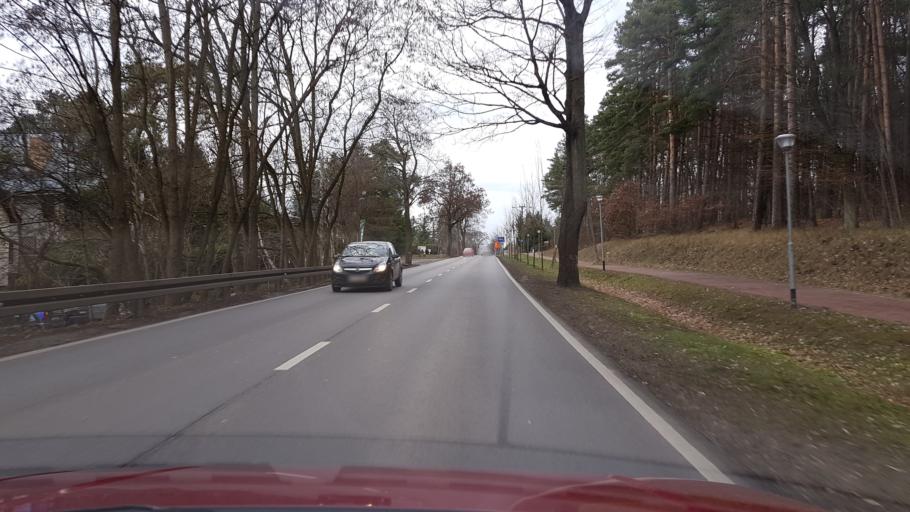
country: PL
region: West Pomeranian Voivodeship
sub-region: Szczecin
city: Szczecin
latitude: 53.4901
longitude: 14.4813
